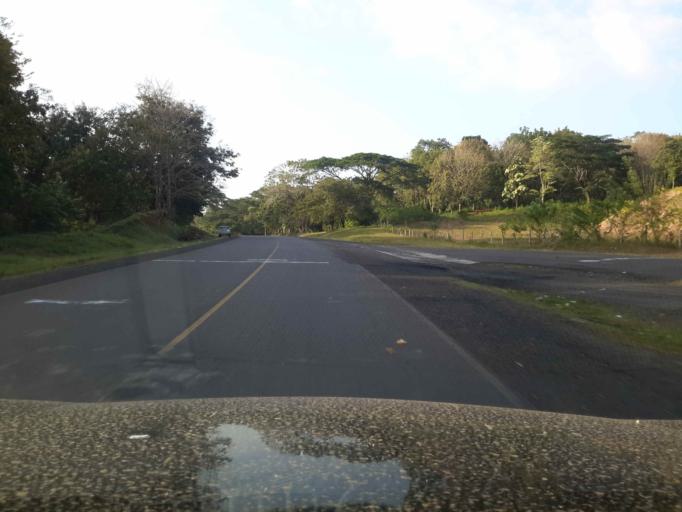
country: NI
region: Rio San Juan
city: San Miguelito
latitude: 11.3619
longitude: -84.7650
